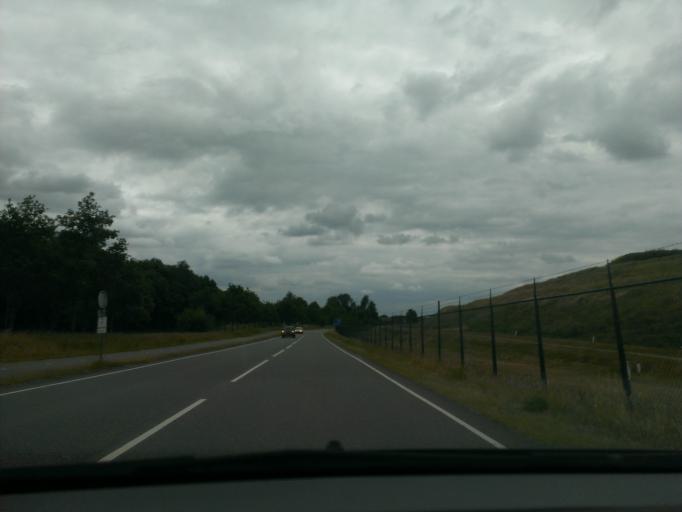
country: NL
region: Gelderland
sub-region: Gemeente Voorst
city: Twello
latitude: 52.2043
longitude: 6.0865
